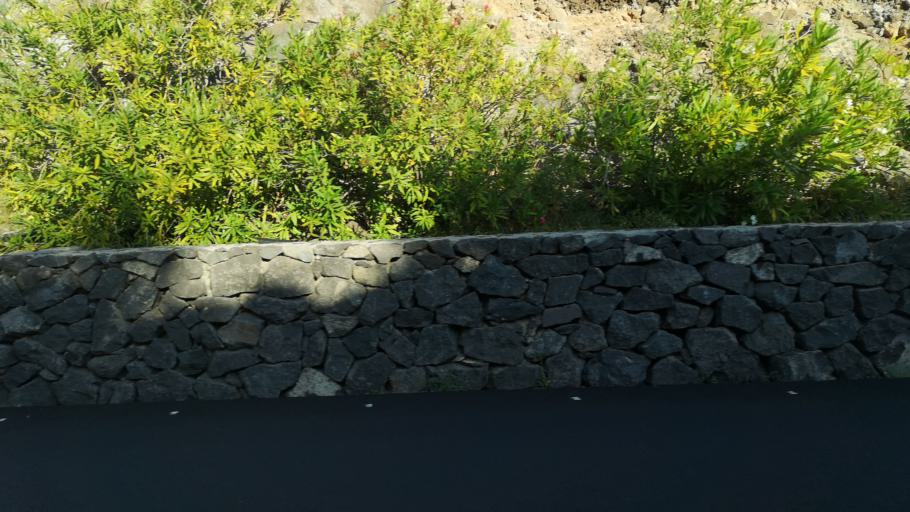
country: ES
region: Canary Islands
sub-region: Provincia de Santa Cruz de Tenerife
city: Alajero
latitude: 28.0395
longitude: -17.1956
